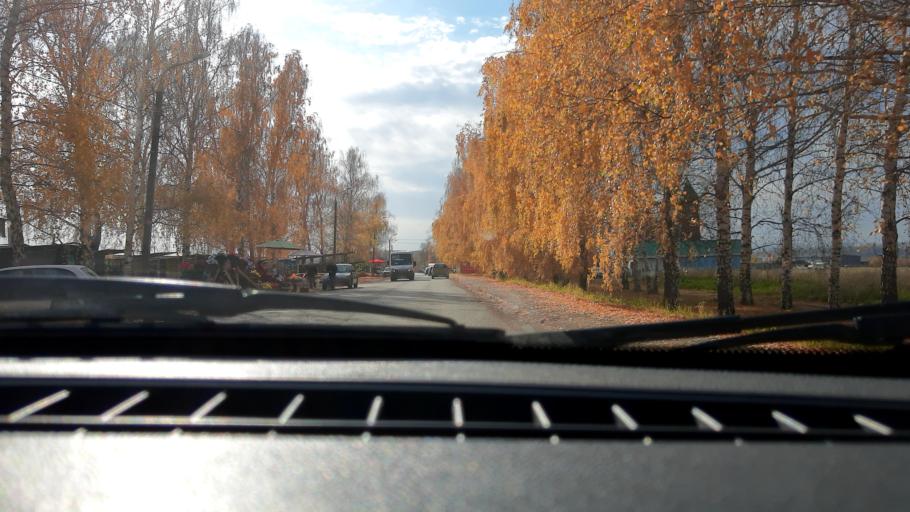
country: RU
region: Bashkortostan
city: Ufa
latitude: 54.8486
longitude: 56.1538
